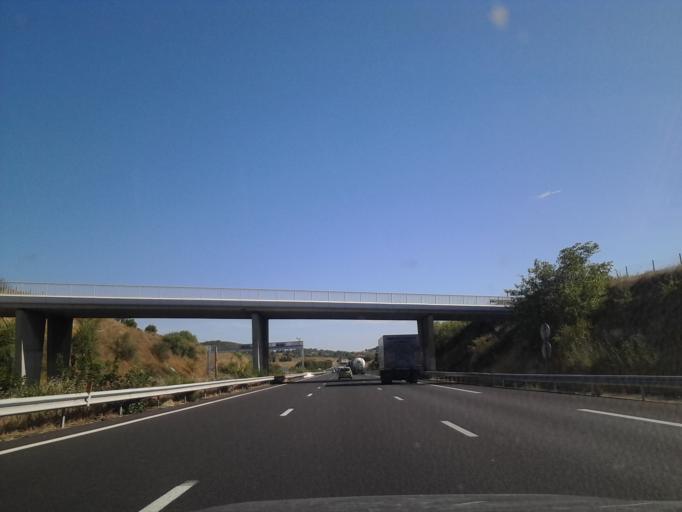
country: FR
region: Languedoc-Roussillon
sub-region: Departement de l'Herault
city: Lespignan
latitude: 43.2762
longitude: 3.1835
